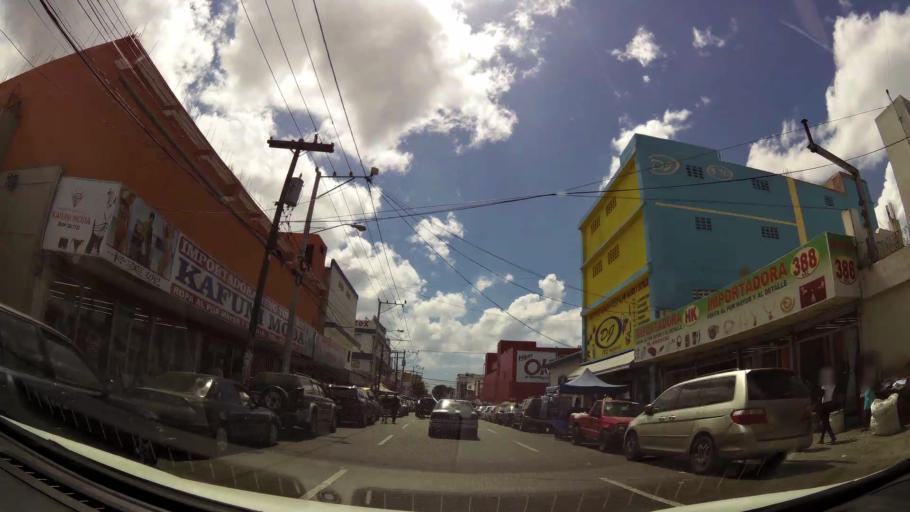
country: DO
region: Nacional
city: San Carlos
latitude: 18.4891
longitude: -69.8960
